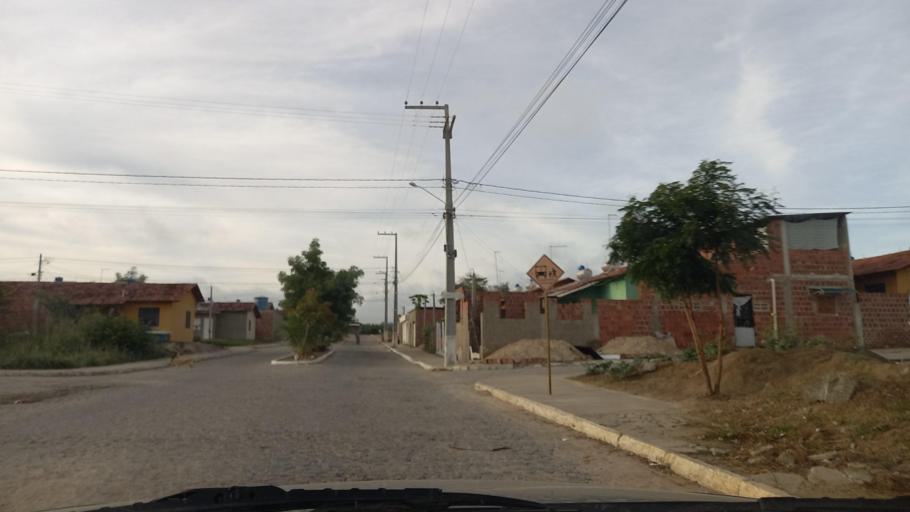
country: BR
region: Pernambuco
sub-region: Bezerros
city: Bezerros
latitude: -8.2170
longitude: -35.7399
